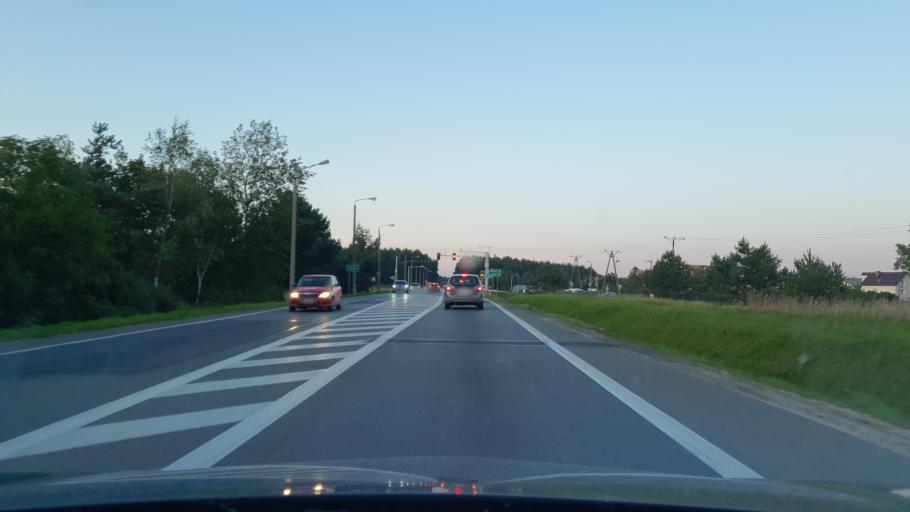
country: PL
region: Pomeranian Voivodeship
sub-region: Powiat leborski
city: Lebork
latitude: 54.5446
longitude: 17.7876
